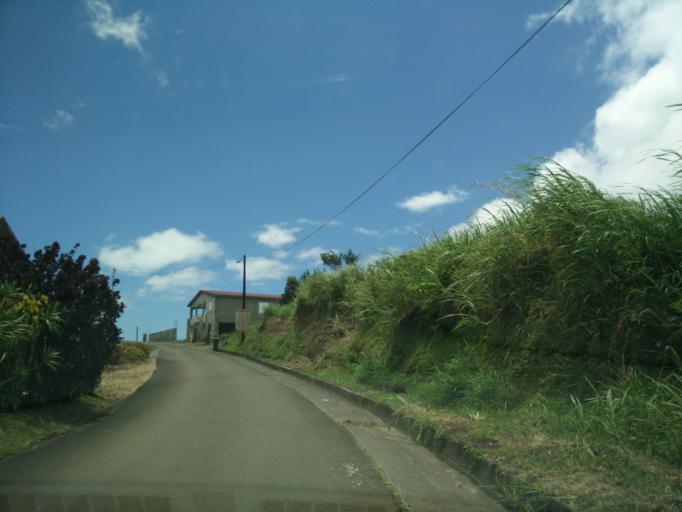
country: MQ
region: Martinique
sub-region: Martinique
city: Le Morne-Rouge
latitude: 14.7847
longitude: -61.1394
